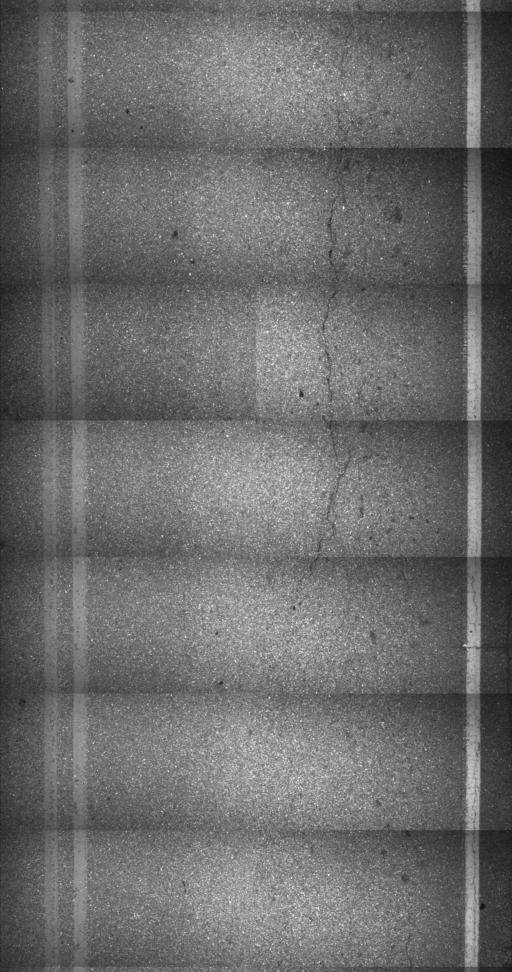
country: US
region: Vermont
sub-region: Orange County
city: Randolph
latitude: 43.9722
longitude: -72.8432
